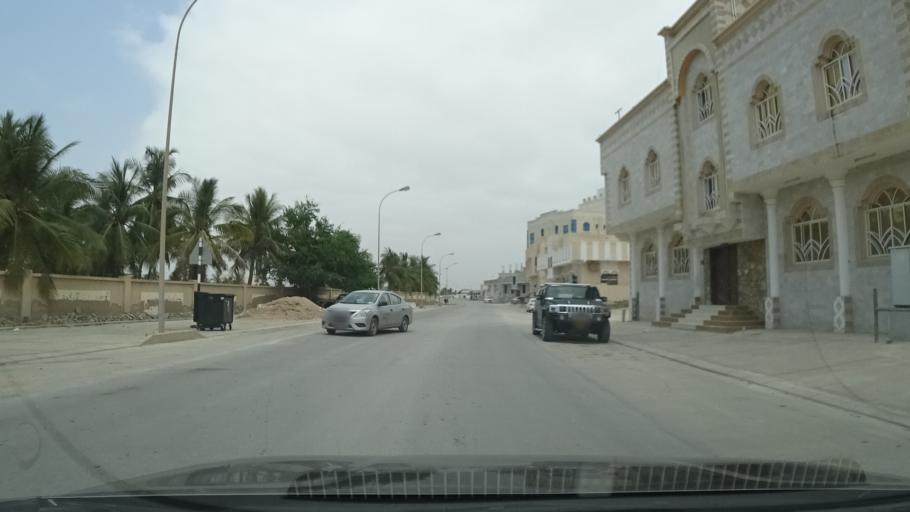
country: OM
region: Zufar
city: Salalah
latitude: 17.0229
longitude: 54.1642
